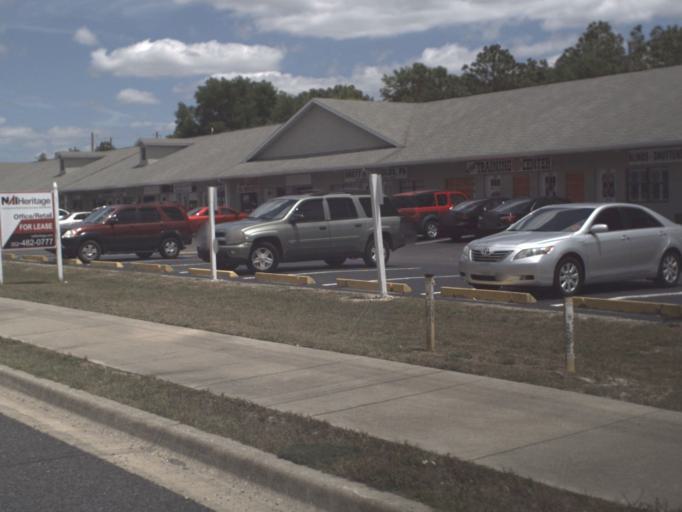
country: US
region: Florida
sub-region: Marion County
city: Ocala
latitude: 29.0705
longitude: -82.2660
